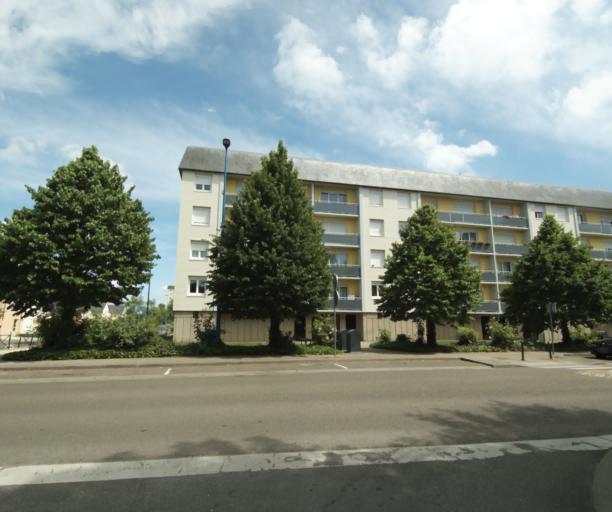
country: FR
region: Centre
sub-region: Departement d'Eure-et-Loir
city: Luce
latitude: 48.4349
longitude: 1.4608
